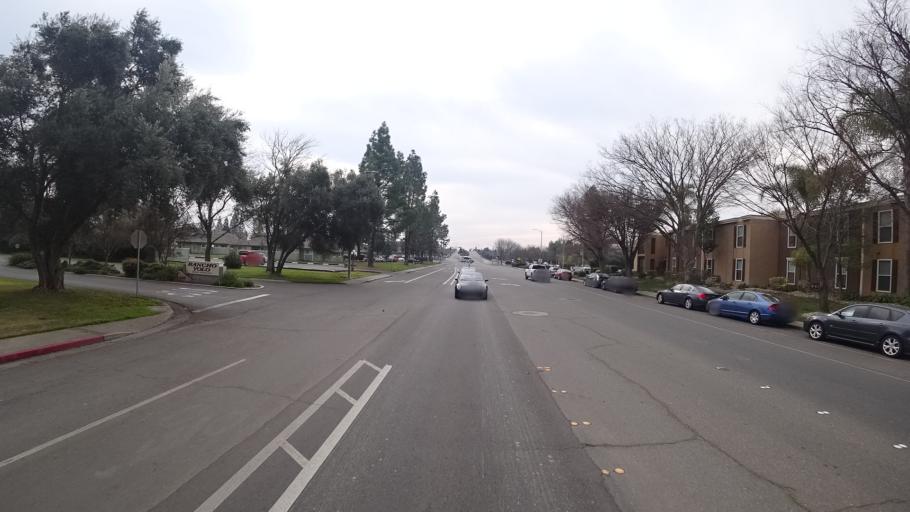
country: US
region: California
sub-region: Yolo County
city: Davis
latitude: 38.5504
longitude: -121.7268
